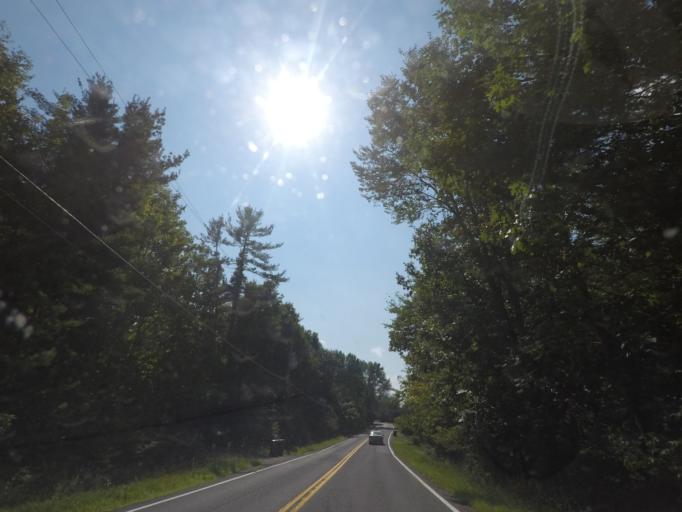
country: US
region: New York
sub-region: Rensselaer County
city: Poestenkill
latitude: 42.8209
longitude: -73.4931
